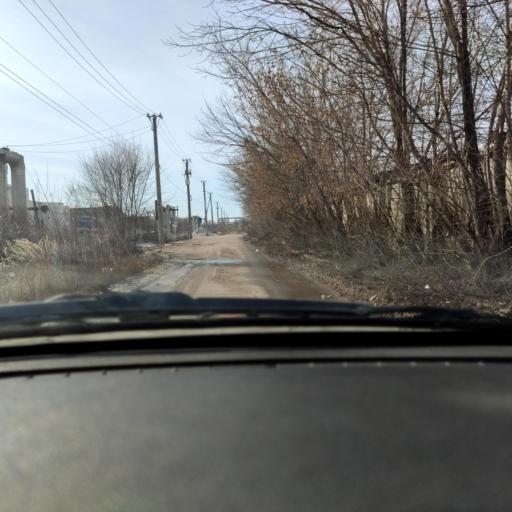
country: RU
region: Samara
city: Tol'yatti
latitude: 53.5761
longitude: 49.2627
